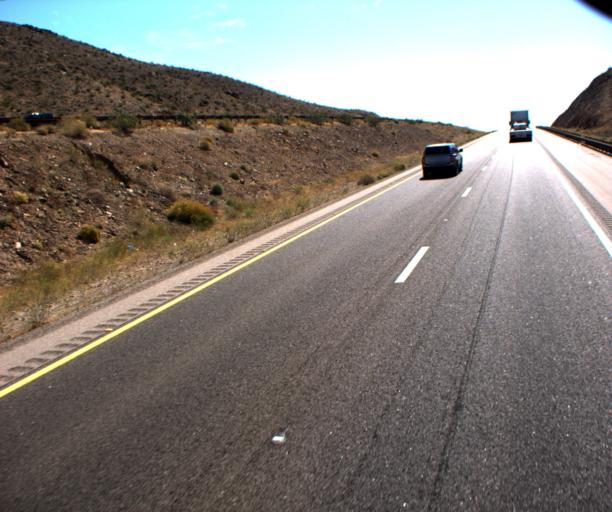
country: US
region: Nevada
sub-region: Clark County
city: Boulder City
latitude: 35.8482
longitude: -114.5864
